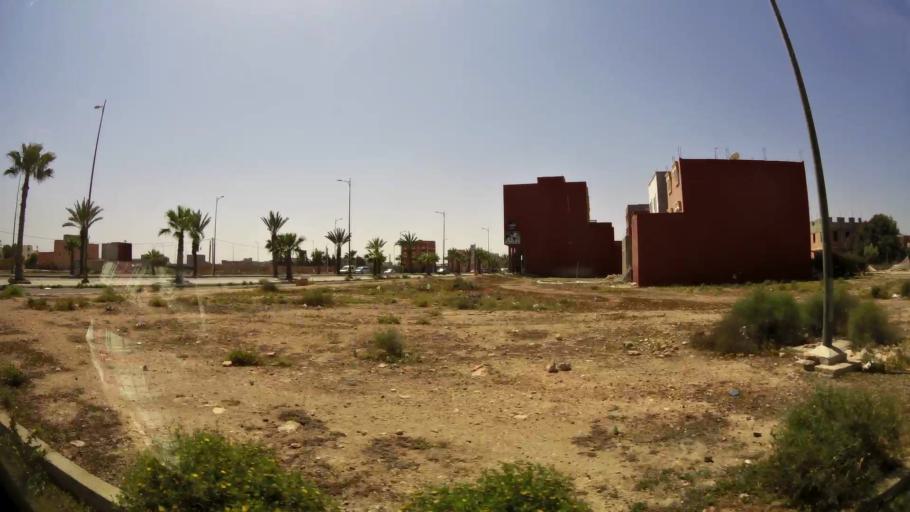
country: MA
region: Souss-Massa-Draa
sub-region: Inezgane-Ait Mellou
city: Inezgane
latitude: 30.3199
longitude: -9.5037
